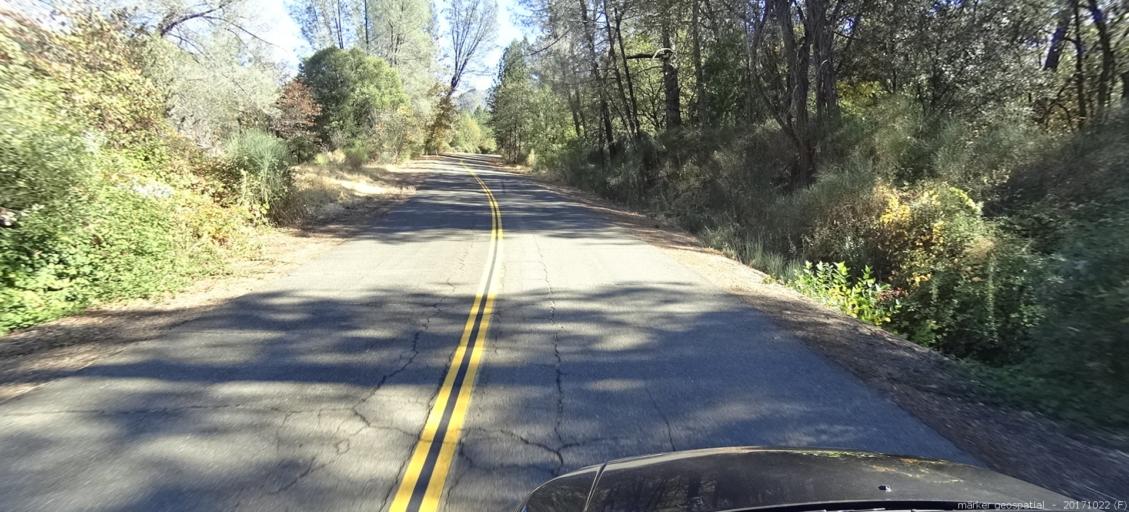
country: US
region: California
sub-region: Shasta County
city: Central Valley (historical)
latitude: 40.9170
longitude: -122.3916
